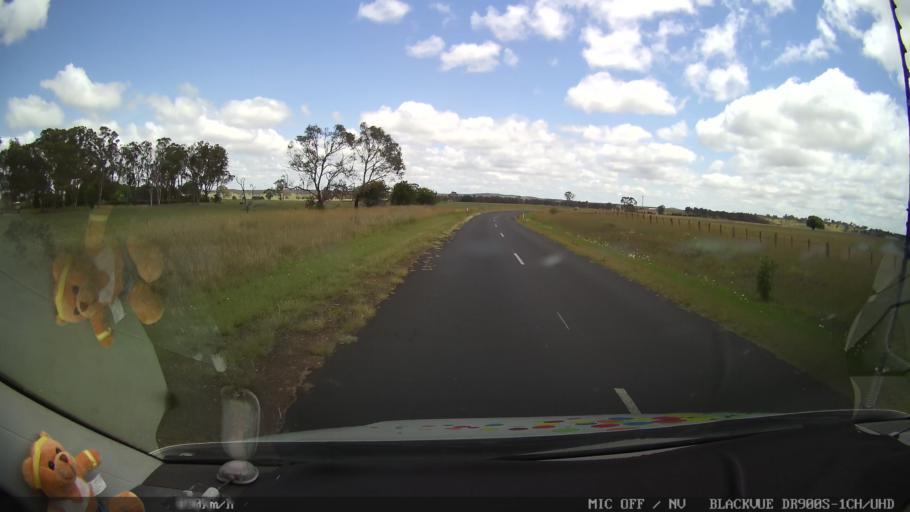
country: AU
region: New South Wales
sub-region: Glen Innes Severn
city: Glen Innes
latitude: -29.6611
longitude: 151.6925
